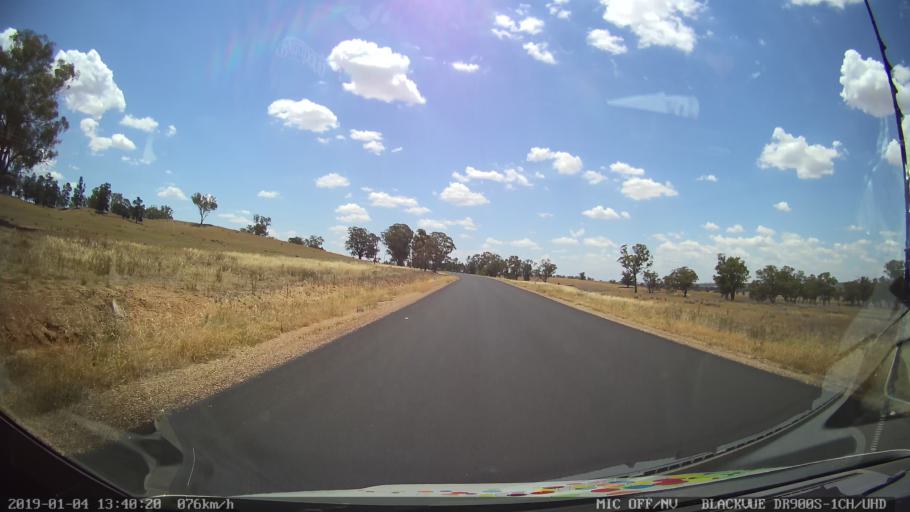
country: AU
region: New South Wales
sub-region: Dubbo Municipality
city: Dubbo
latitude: -32.5153
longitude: 148.5551
